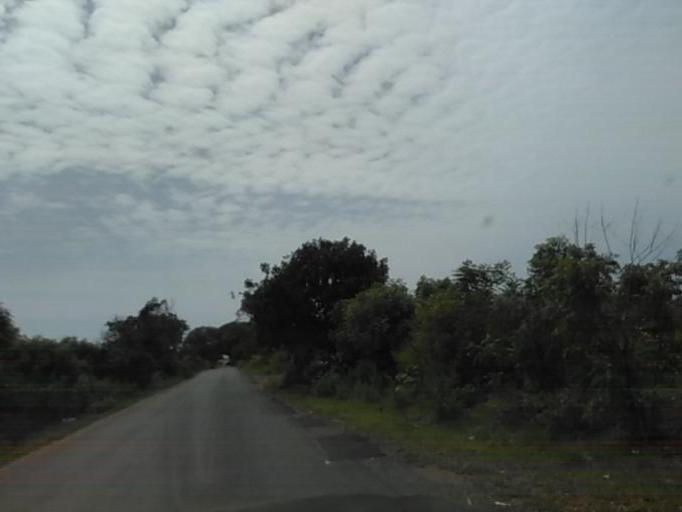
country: GH
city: Akropong
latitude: 6.0930
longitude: 0.0734
